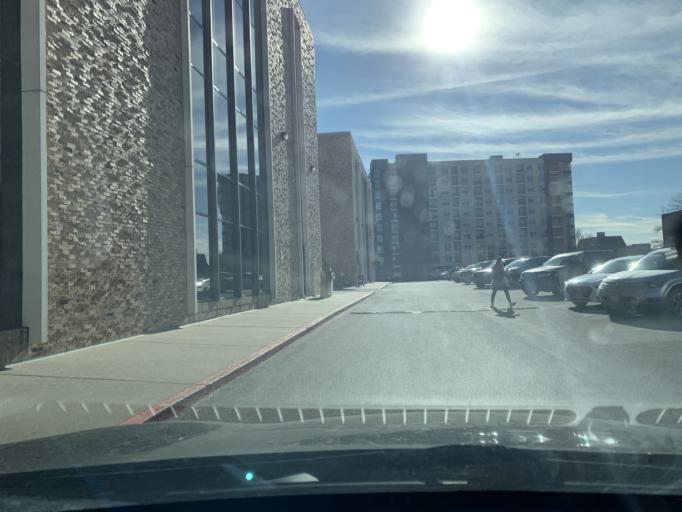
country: US
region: Colorado
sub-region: Denver County
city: Denver
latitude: 39.7544
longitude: -105.0165
